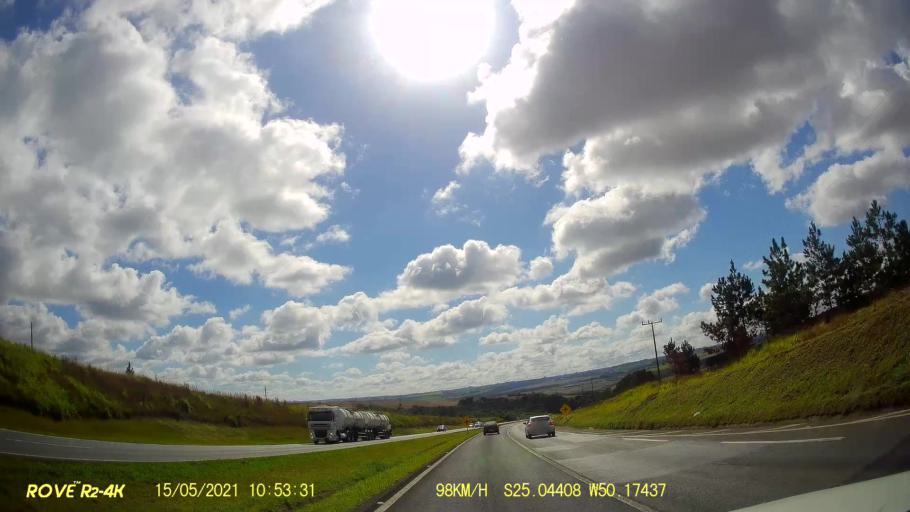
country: BR
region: Parana
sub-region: Ponta Grossa
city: Ponta Grossa
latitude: -25.0443
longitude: -50.1757
